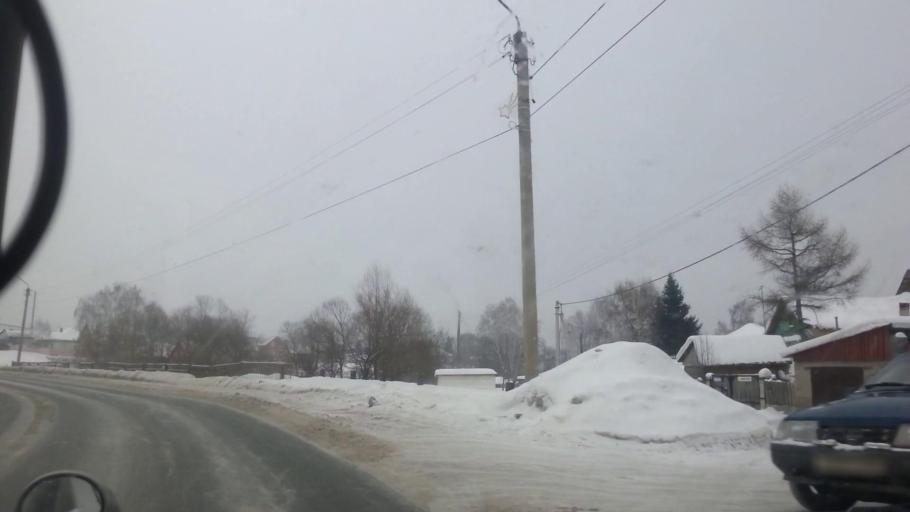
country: RU
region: Altai Krai
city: Vlasikha
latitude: 53.2951
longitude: 83.5792
